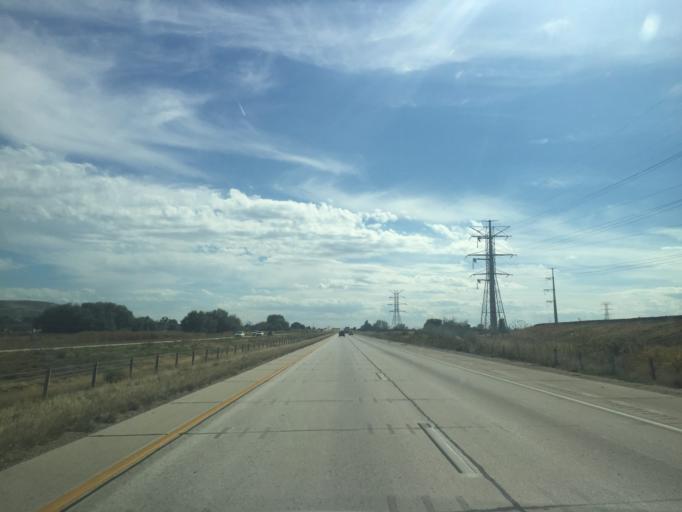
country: US
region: Utah
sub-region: Box Elder County
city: South Willard
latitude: 41.3823
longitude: -112.0422
